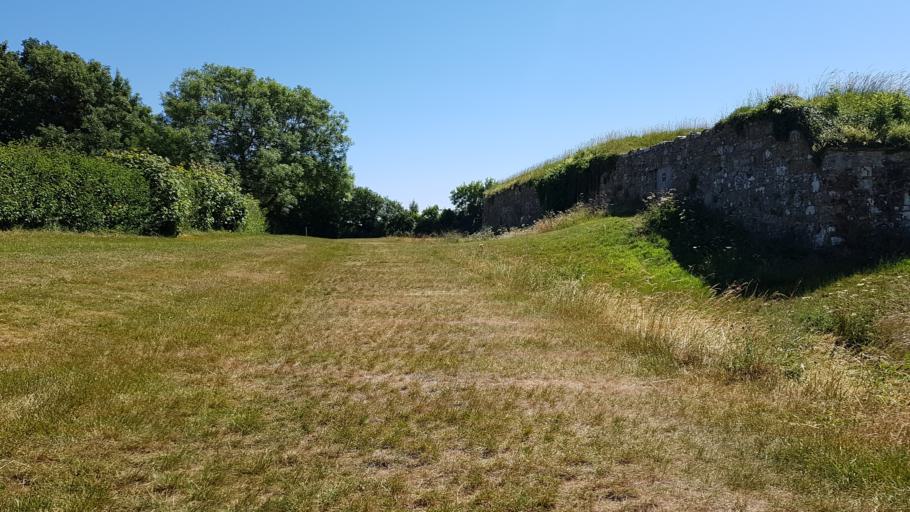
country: GB
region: England
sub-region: Isle of Wight
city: Newport
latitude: 50.6877
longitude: -1.3101
